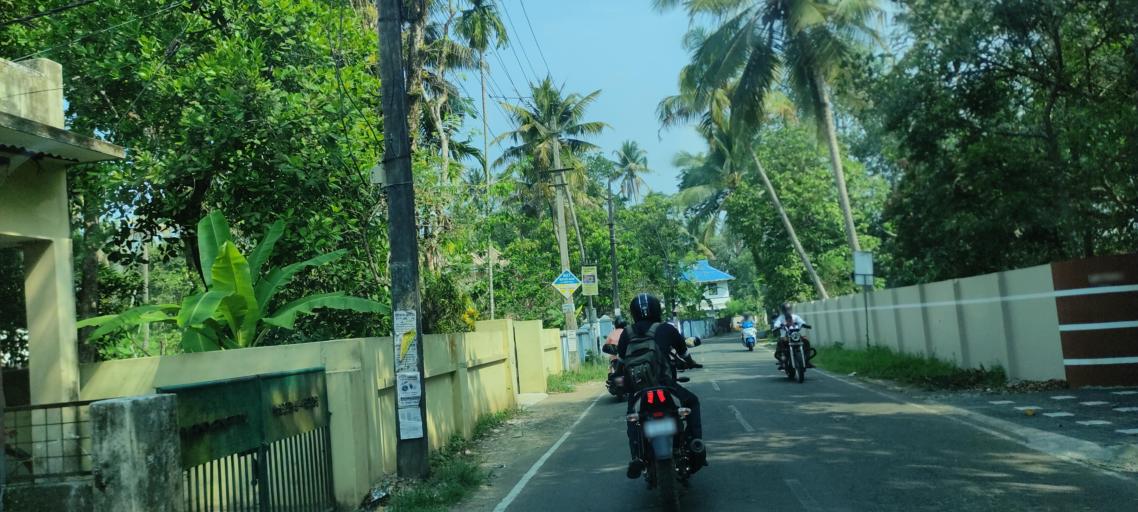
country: IN
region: Kerala
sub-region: Alappuzha
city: Kutiatodu
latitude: 9.7719
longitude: 76.3079
